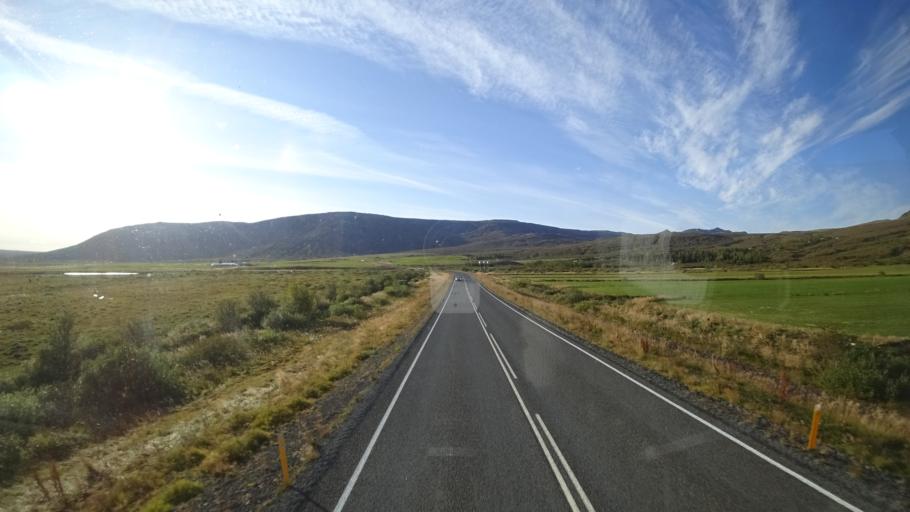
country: IS
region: South
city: Selfoss
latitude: 64.2397
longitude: -20.6619
